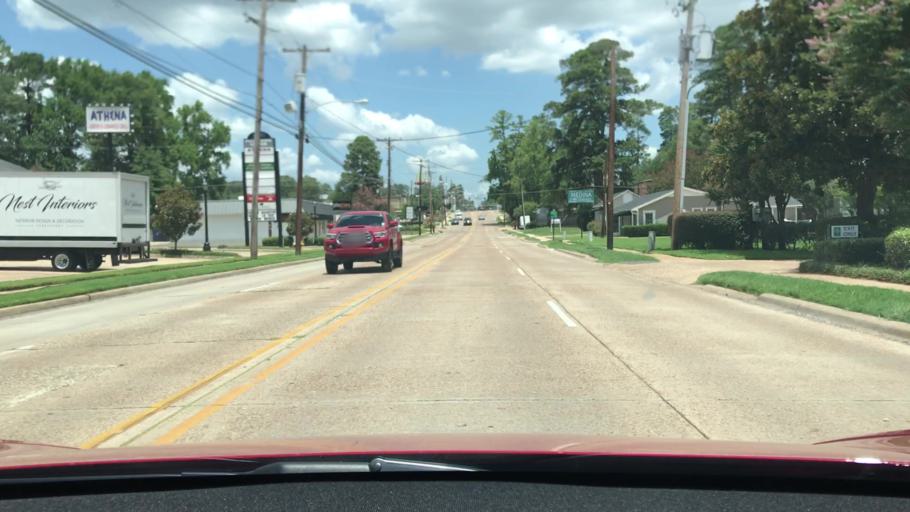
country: US
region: Louisiana
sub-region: Bossier Parish
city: Bossier City
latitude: 32.4513
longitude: -93.7460
